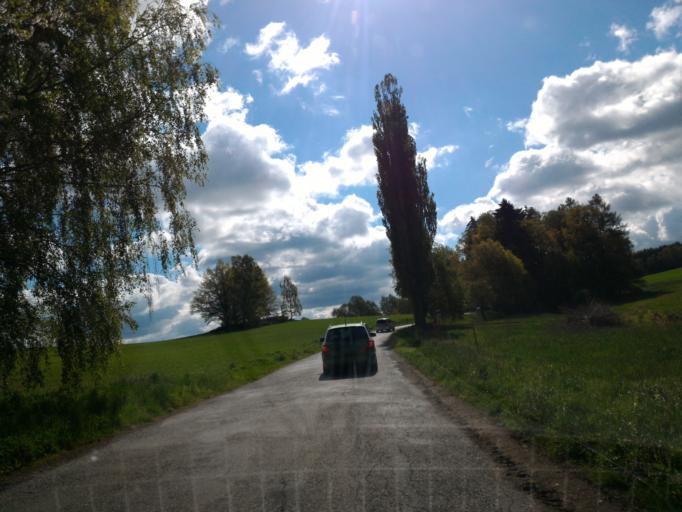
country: CZ
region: Vysocina
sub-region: Okres Havlickuv Brod
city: Svetla nad Sazavou
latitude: 49.6330
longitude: 15.3565
